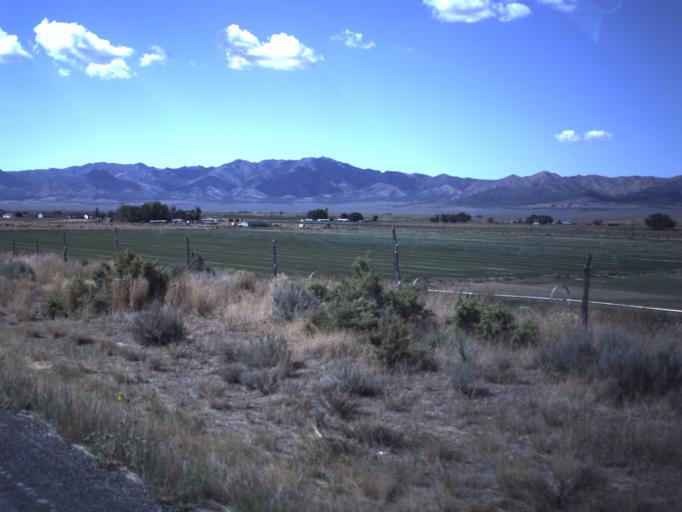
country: US
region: Utah
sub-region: Tooele County
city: Tooele
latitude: 40.1127
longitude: -112.4308
